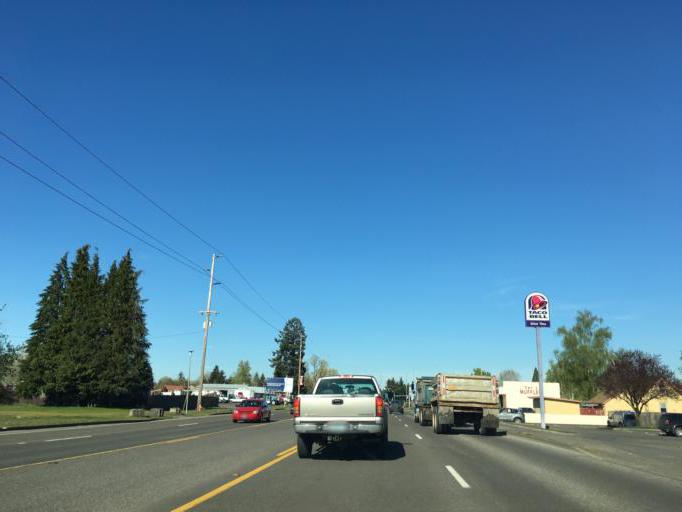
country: US
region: Oregon
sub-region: Clackamas County
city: Canby
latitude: 45.2577
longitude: -122.7013
